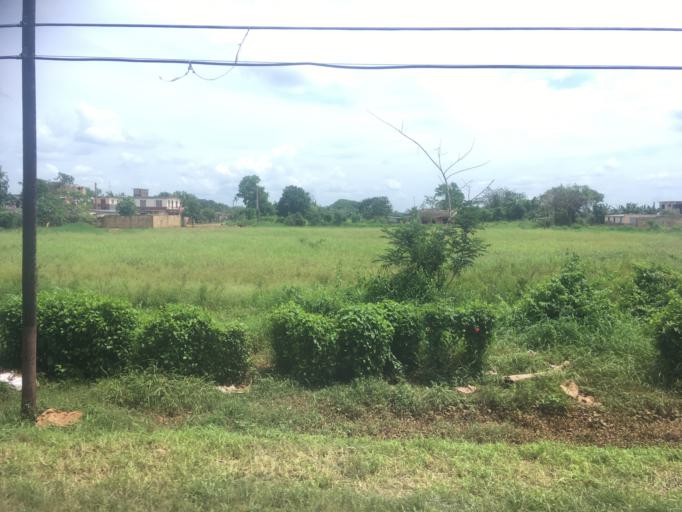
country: CU
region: Matanzas
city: Perico
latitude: 22.7736
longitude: -81.0252
